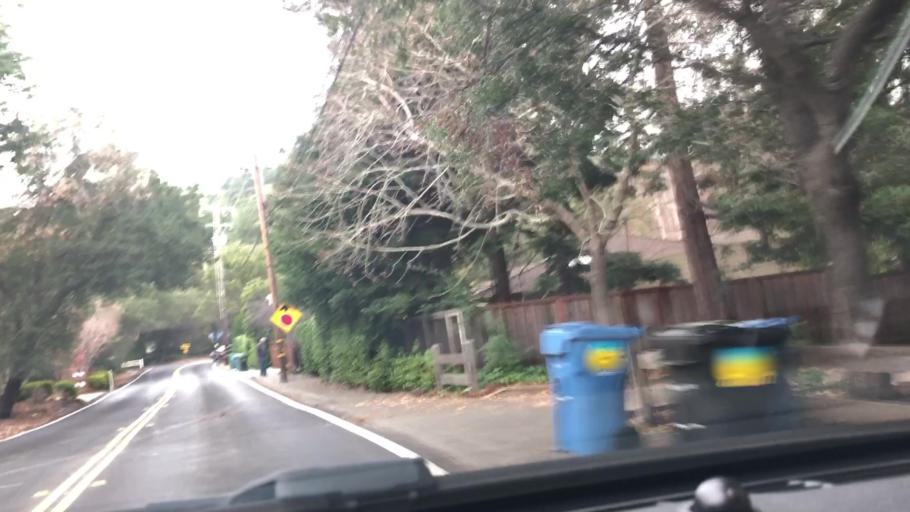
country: US
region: California
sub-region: Contra Costa County
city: Orinda
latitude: 37.9056
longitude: -122.1530
